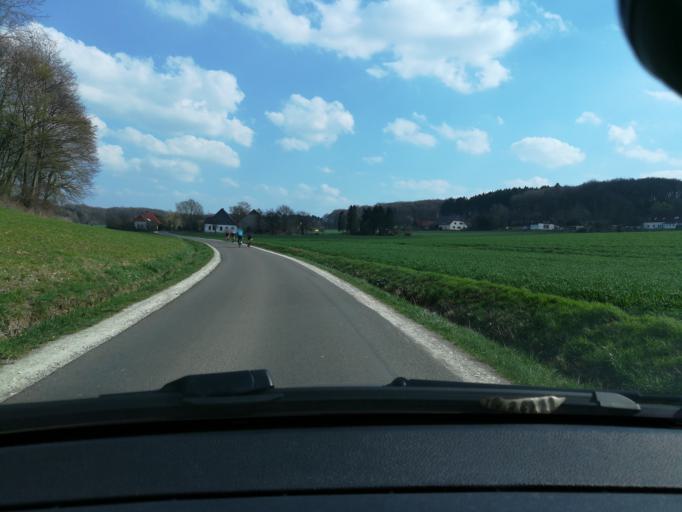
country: DE
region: North Rhine-Westphalia
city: Borgholzhausen
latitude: 52.1001
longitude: 8.3204
